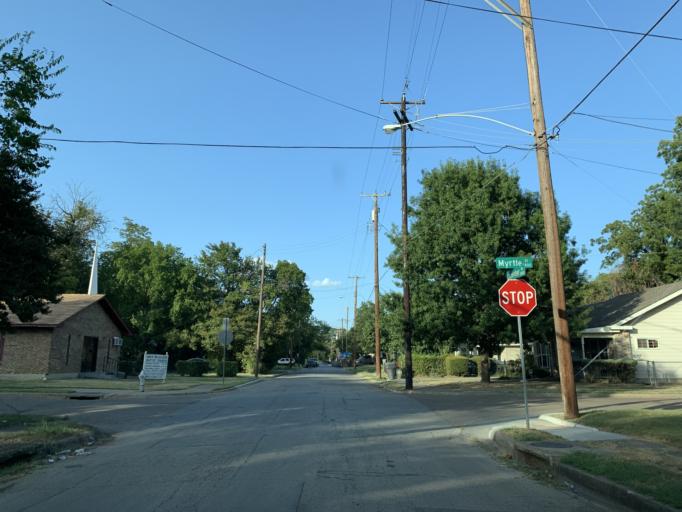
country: US
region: Texas
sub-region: Dallas County
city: Dallas
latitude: 32.7567
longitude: -96.7570
